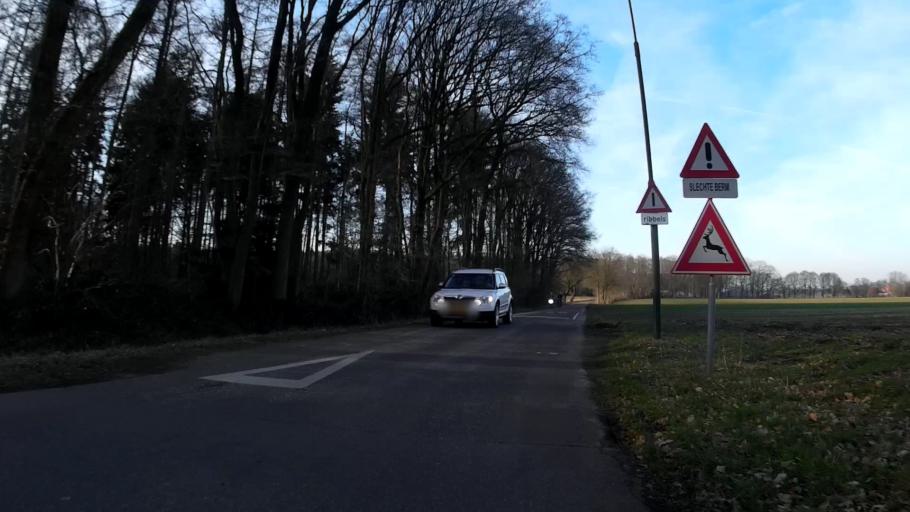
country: NL
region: Utrecht
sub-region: Gemeente Rhenen
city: Rhenen
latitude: 51.9779
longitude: 5.5656
